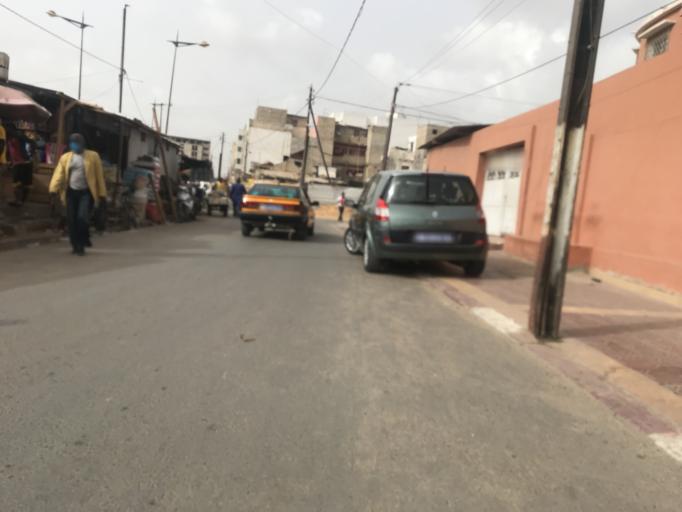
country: SN
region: Dakar
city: Dakar
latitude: 14.6792
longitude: -17.4566
